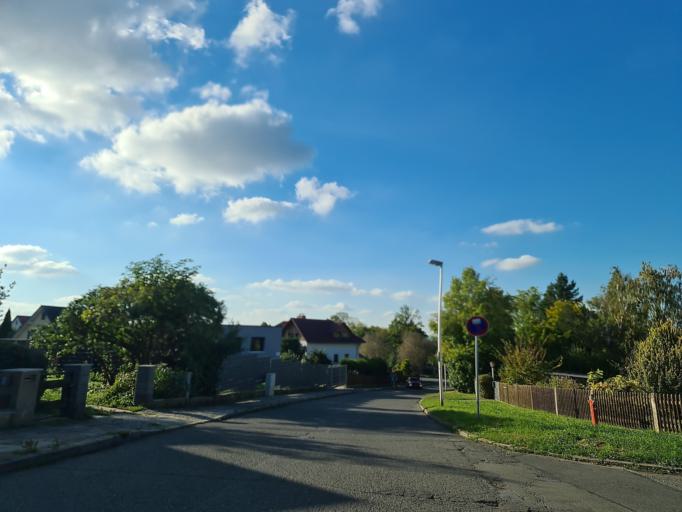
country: DE
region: Thuringia
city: Gera
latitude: 50.9019
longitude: 12.0772
